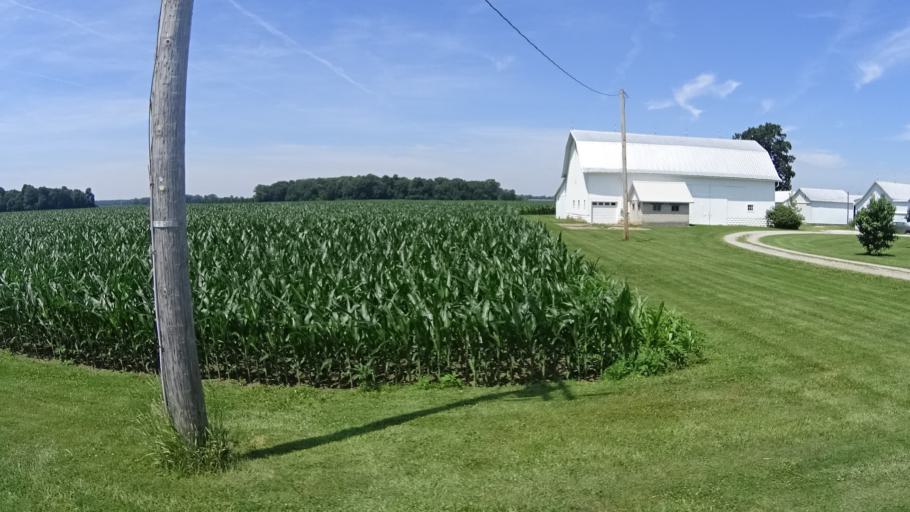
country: US
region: Ohio
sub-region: Erie County
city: Huron
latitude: 41.3548
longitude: -82.5172
